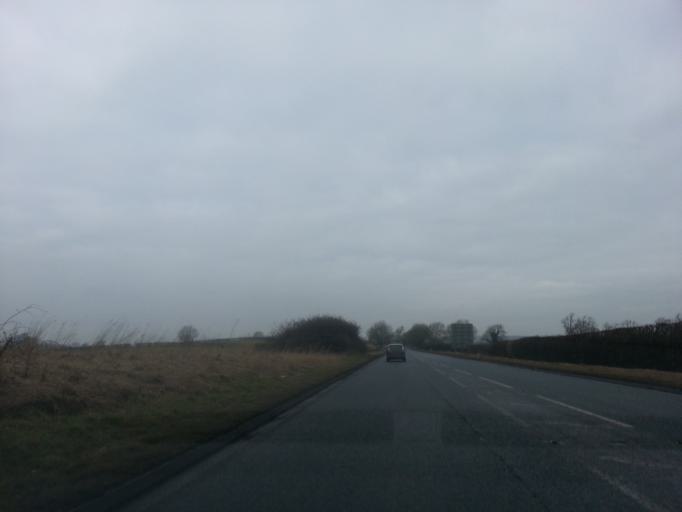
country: GB
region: England
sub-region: Darlington
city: Heighington
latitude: 54.5780
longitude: -1.6162
